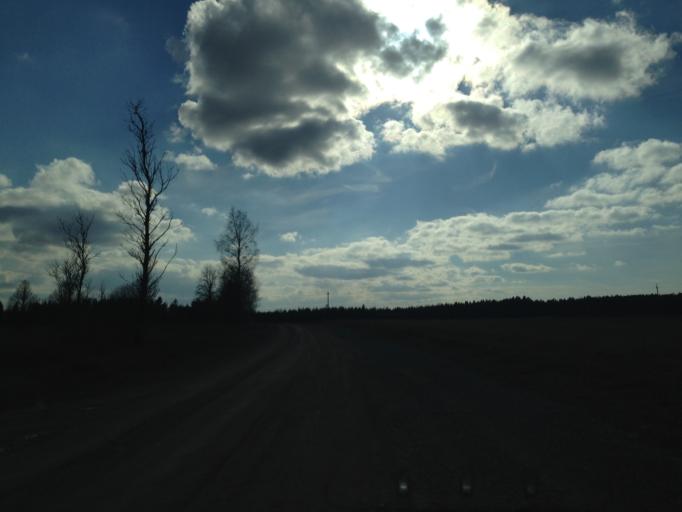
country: EE
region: Harju
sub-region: Nissi vald
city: Riisipere
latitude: 59.1246
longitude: 24.3637
